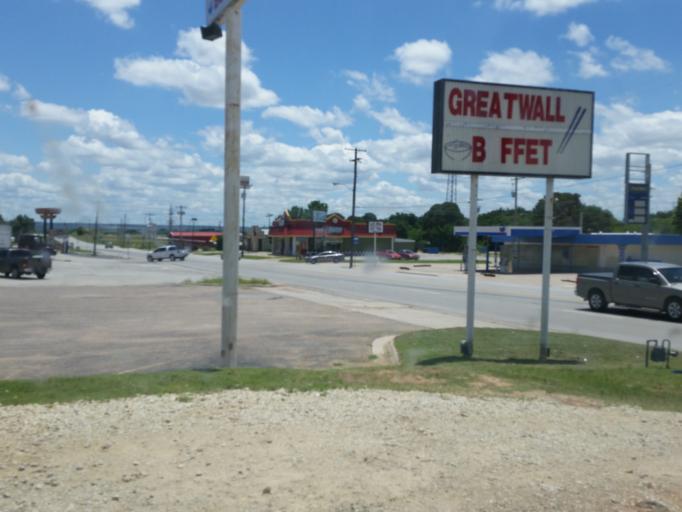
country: US
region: Texas
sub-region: Nolan County
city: Sweetwater
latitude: 32.4493
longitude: -100.3980
